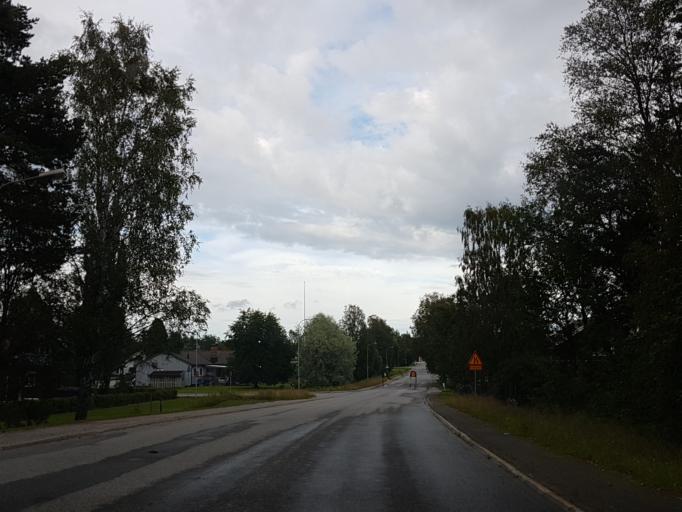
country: SE
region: Vaesterbotten
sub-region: Umea Kommun
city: Saevar
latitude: 63.8988
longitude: 20.5426
